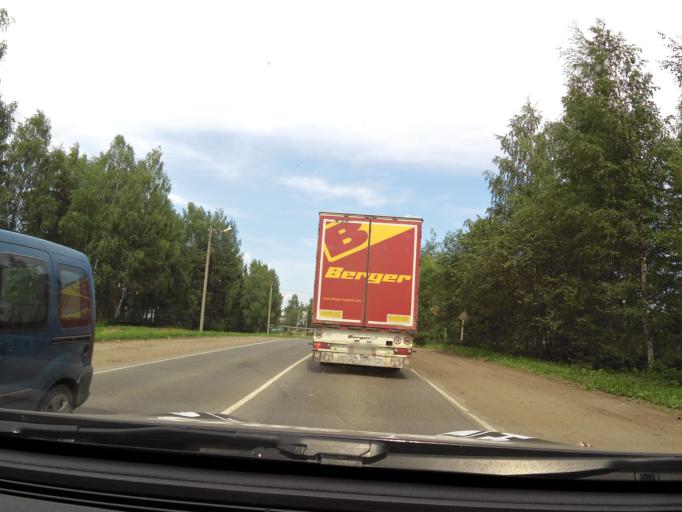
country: RU
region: Kirov
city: Stulovo
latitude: 58.7174
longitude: 50.1314
